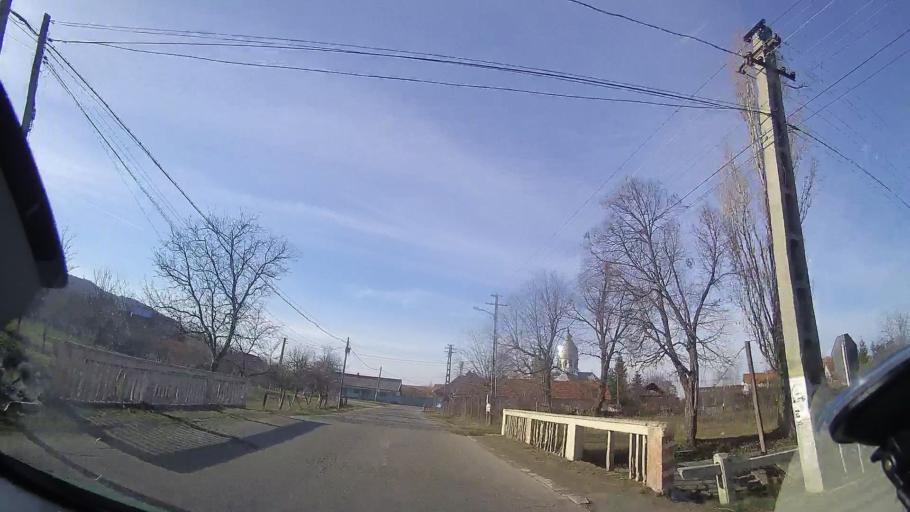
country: RO
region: Bihor
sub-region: Comuna Astileu
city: Astileu
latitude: 47.0283
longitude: 22.3931
